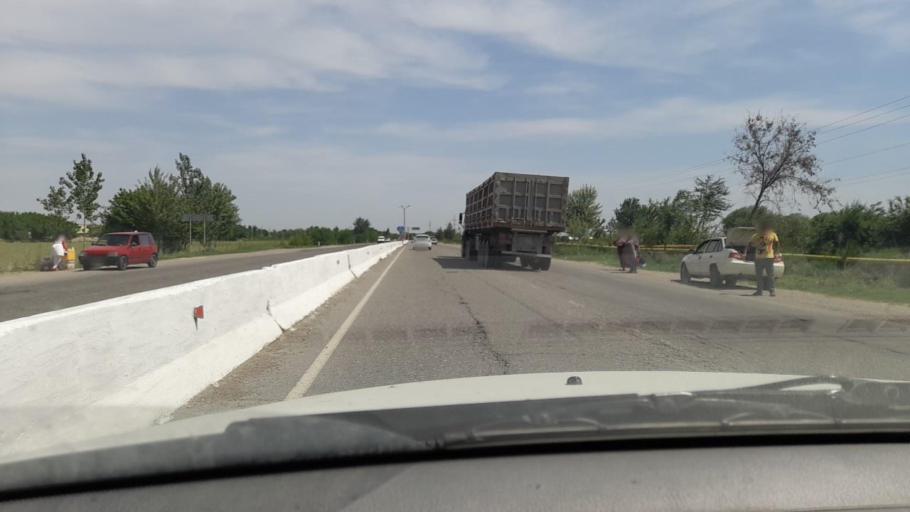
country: UZ
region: Bukhara
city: Wobkent
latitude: 40.0034
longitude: 64.5198
